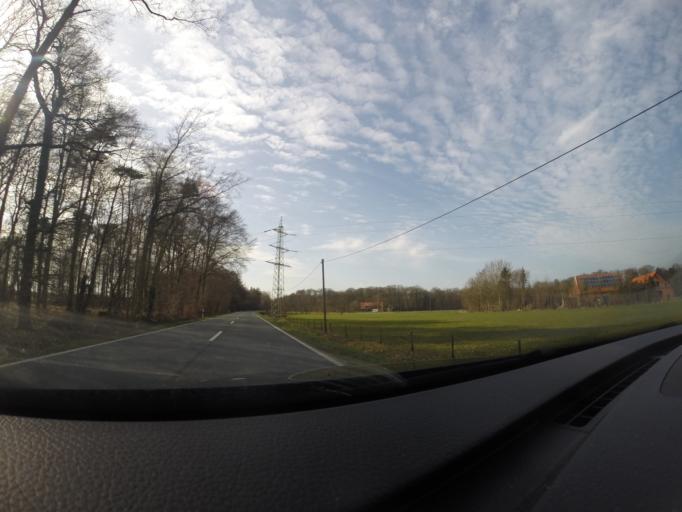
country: DE
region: North Rhine-Westphalia
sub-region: Regierungsbezirk Munster
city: Legden
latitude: 52.0280
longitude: 7.0800
